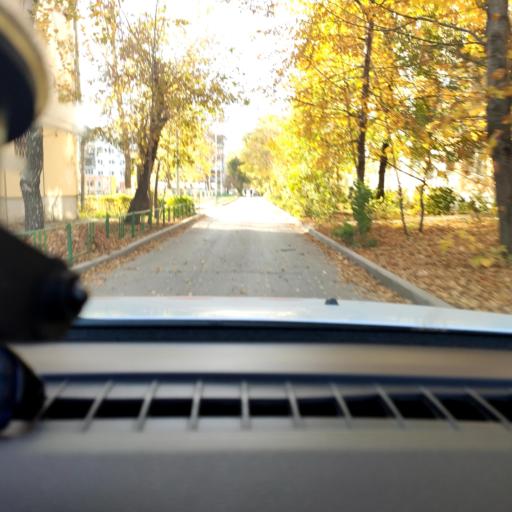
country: RU
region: Samara
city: Samara
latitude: 53.1992
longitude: 50.1707
